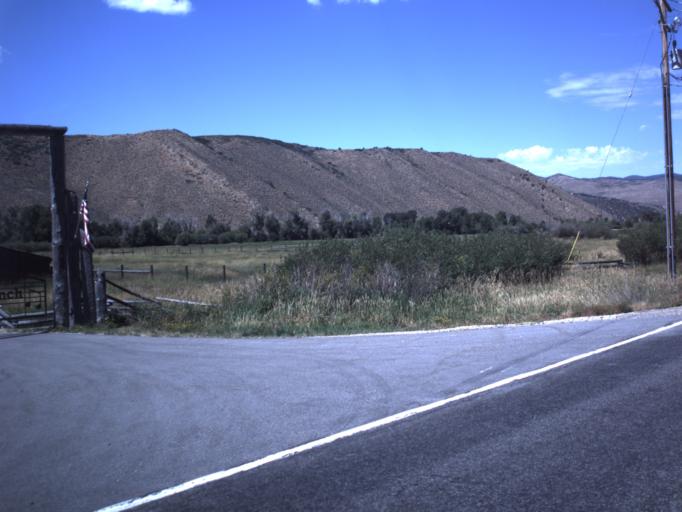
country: US
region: Utah
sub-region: Summit County
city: Oakley
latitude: 40.7447
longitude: -111.3596
